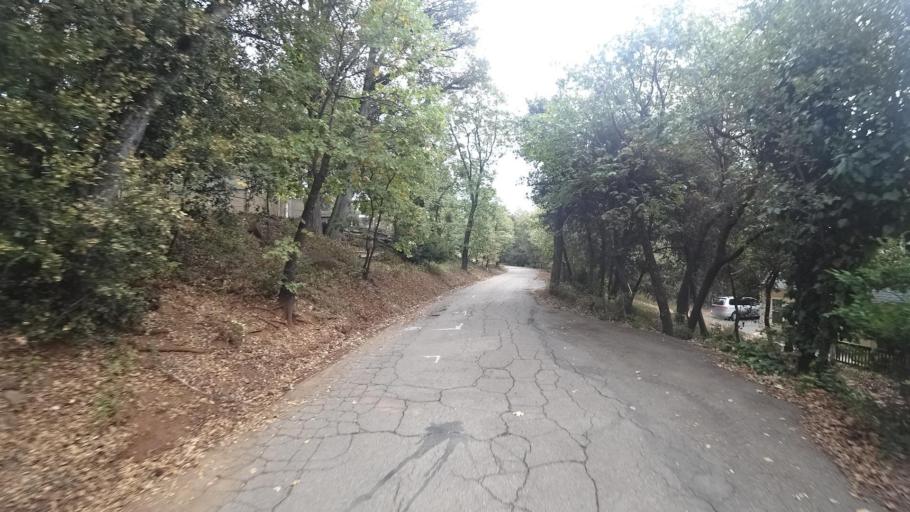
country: US
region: California
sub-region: San Diego County
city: Julian
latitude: 33.0481
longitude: -116.6305
